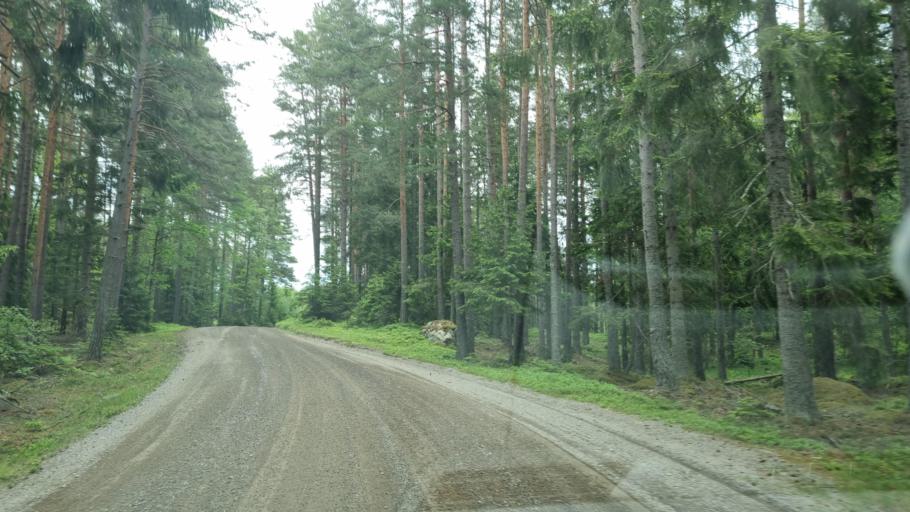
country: SE
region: OEstergoetland
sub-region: Atvidabergs Kommun
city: Atvidaberg
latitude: 58.2586
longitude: 16.0467
